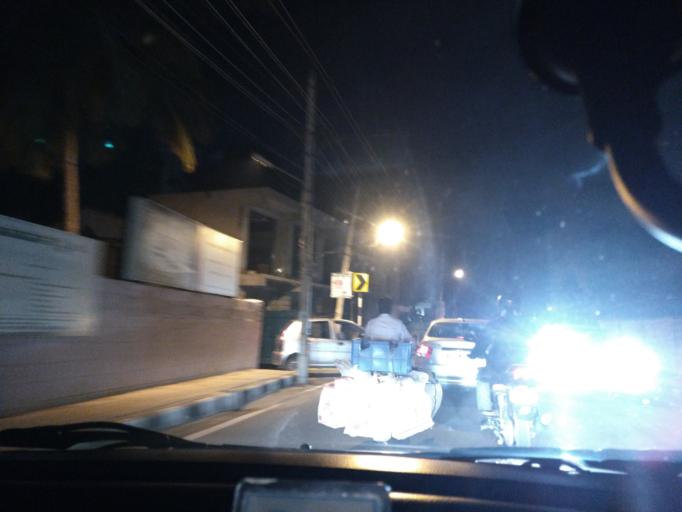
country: IN
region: Karnataka
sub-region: Bangalore Urban
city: Bangalore
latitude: 12.9042
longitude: 77.6622
